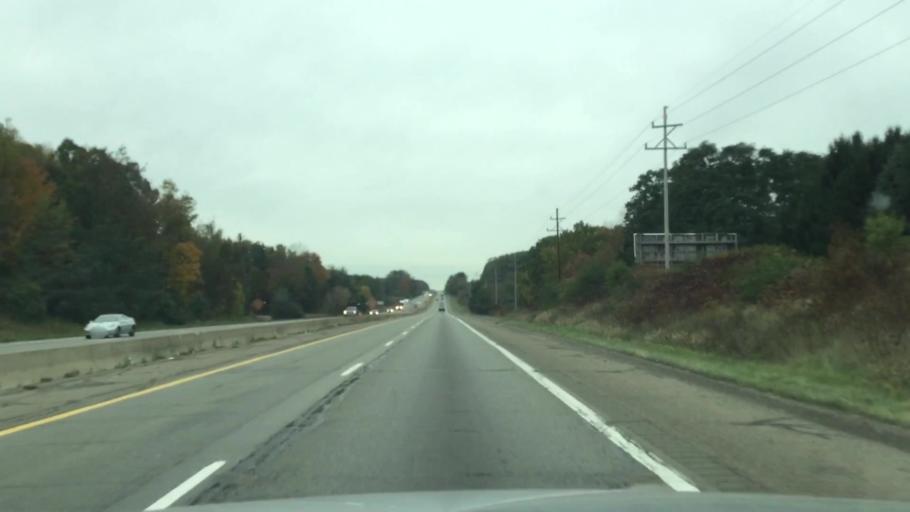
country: US
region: Michigan
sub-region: Jackson County
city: Spring Arbor
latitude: 42.2691
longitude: -84.5016
